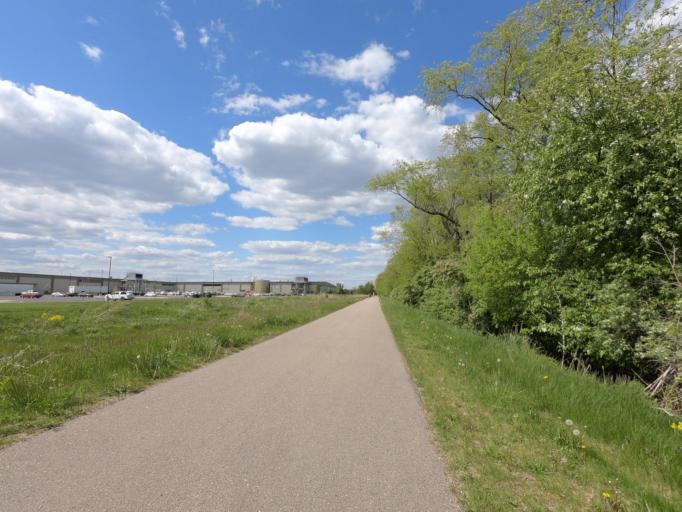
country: US
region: Wisconsin
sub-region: Dane County
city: Fitchburg
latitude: 43.0064
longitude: -89.4607
